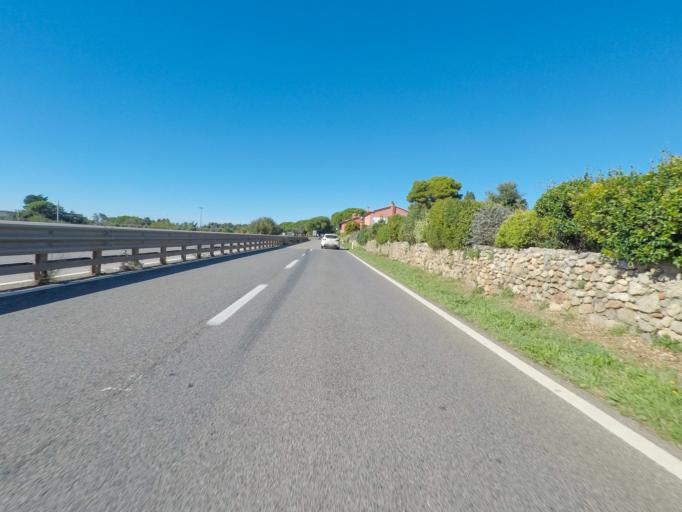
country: IT
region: Tuscany
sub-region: Provincia di Grosseto
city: Orbetello Scalo
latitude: 42.4351
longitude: 11.2807
